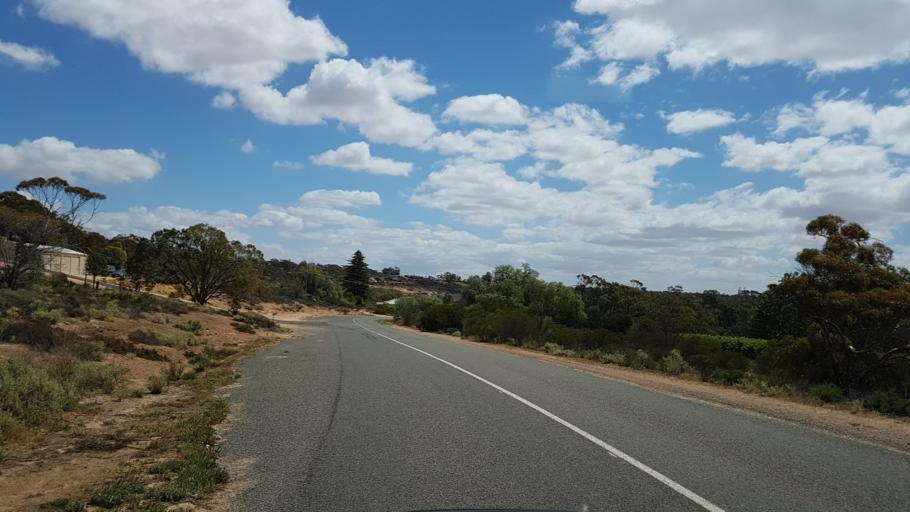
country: AU
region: South Australia
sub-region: Loxton Waikerie
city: Waikerie
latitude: -34.1843
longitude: 140.0175
